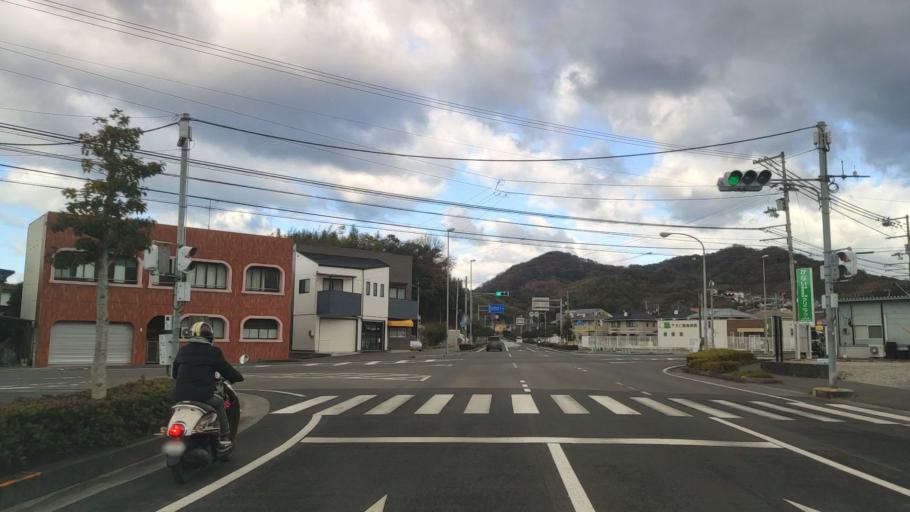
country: JP
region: Ehime
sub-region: Shikoku-chuo Shi
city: Matsuyama
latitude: 33.8717
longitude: 132.7201
